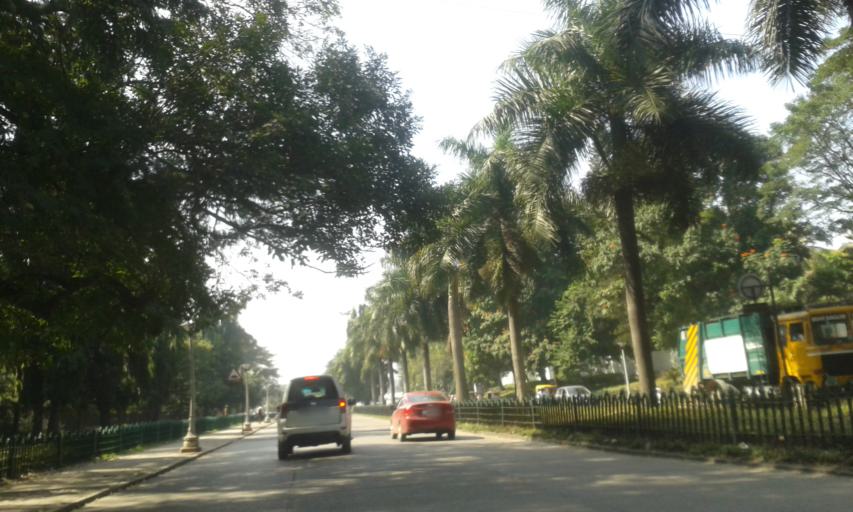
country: IN
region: Karnataka
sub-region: Bangalore Urban
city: Bangalore
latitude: 12.9817
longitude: 77.5947
